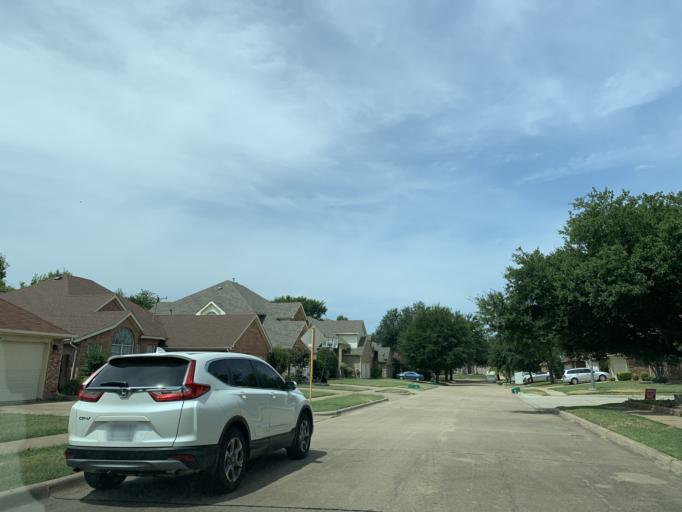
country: US
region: Texas
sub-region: Dallas County
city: Cedar Hill
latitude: 32.6553
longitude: -97.0076
